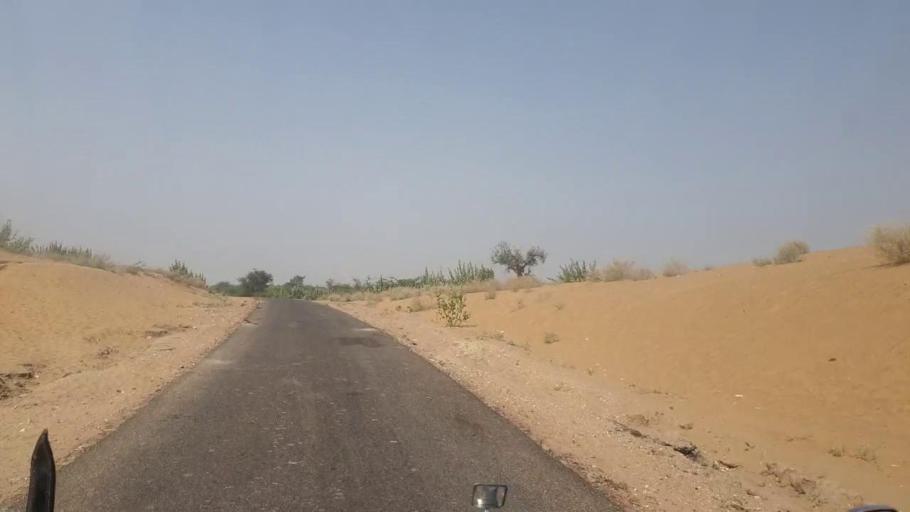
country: PK
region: Sindh
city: Islamkot
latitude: 25.1112
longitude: 70.1999
